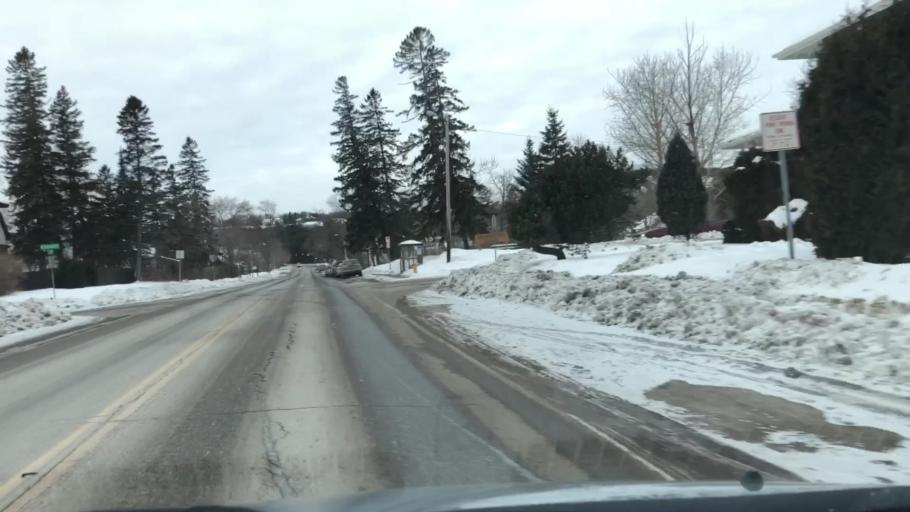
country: US
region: Minnesota
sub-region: Saint Louis County
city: Arnold
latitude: 46.8263
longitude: -92.0362
